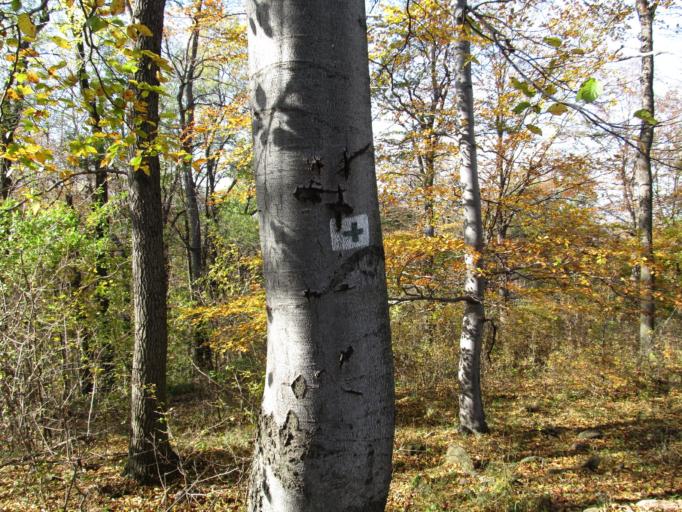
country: SK
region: Nitriansky
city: Sahy
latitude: 47.9739
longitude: 18.9402
